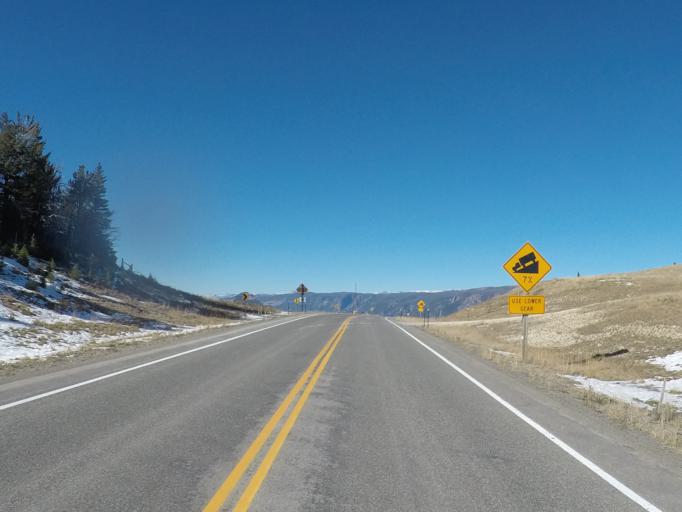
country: US
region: Wyoming
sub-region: Park County
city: Cody
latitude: 44.7445
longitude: -109.3823
